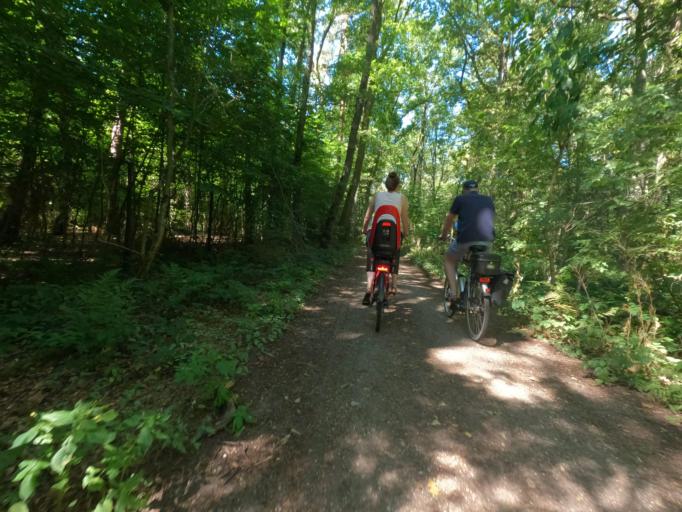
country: DE
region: North Rhine-Westphalia
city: Wegberg
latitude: 51.1495
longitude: 6.2998
